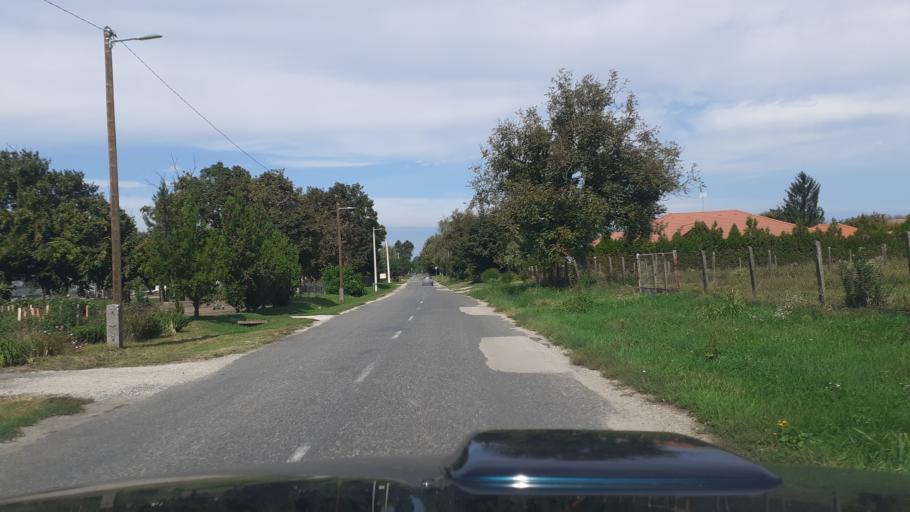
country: HU
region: Fejer
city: Seregelyes
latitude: 47.1180
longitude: 18.5834
